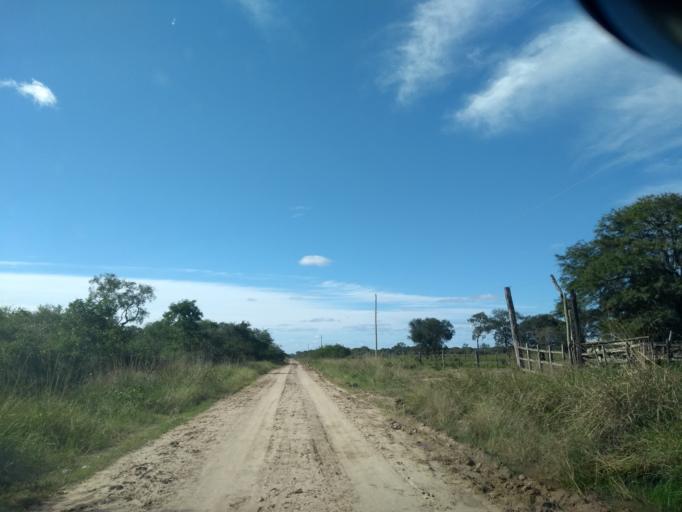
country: AR
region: Chaco
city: Colonia Benitez
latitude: -27.2908
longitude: -58.9356
